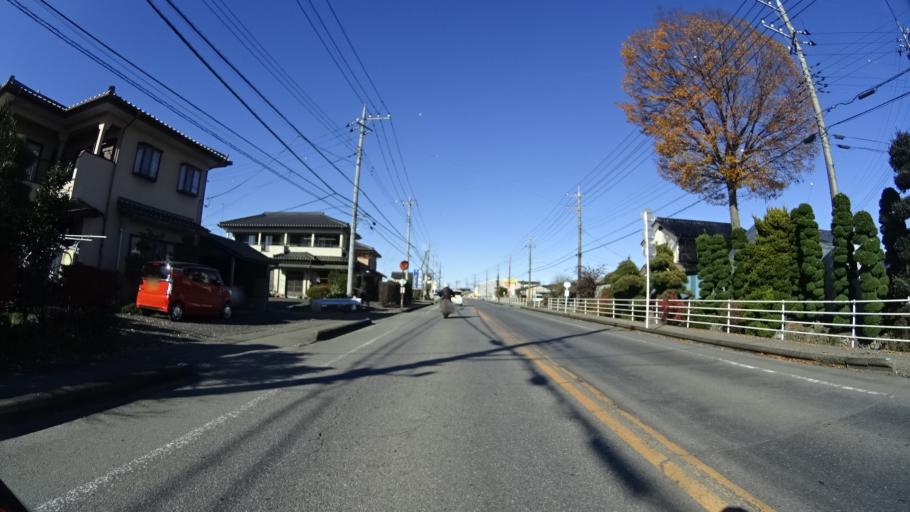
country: JP
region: Tochigi
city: Kanuma
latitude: 36.5226
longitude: 139.7504
